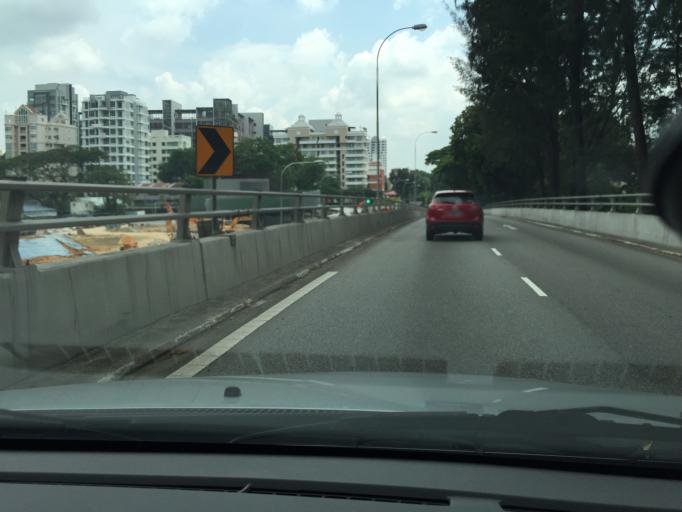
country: SG
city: Singapore
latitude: 1.3131
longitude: 103.8389
